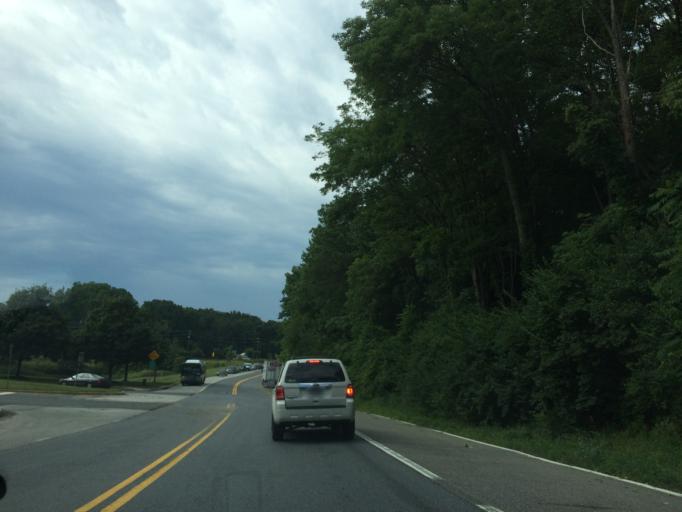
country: US
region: Maryland
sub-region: Montgomery County
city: Clarksburg
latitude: 39.2360
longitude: -77.2831
